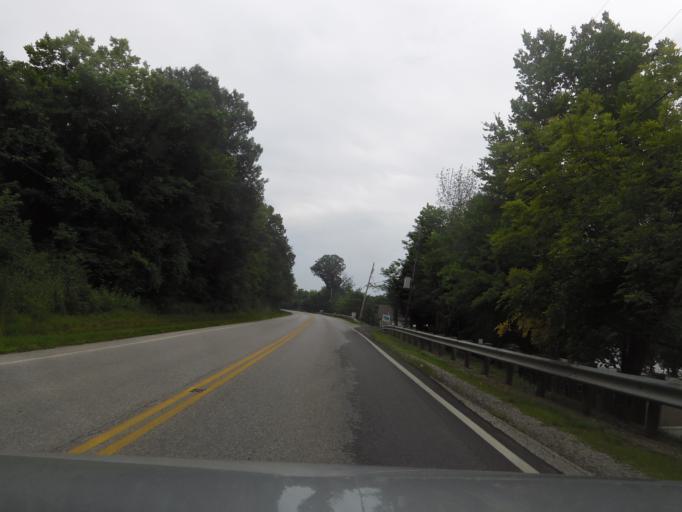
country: US
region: Ohio
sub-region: Brown County
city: Ripley
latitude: 38.7095
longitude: -83.8174
